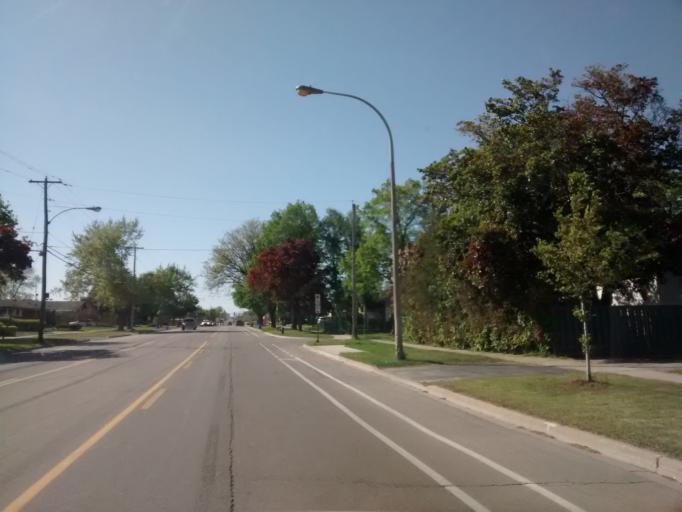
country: CA
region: Ontario
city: Burlington
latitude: 43.3654
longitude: -79.7512
